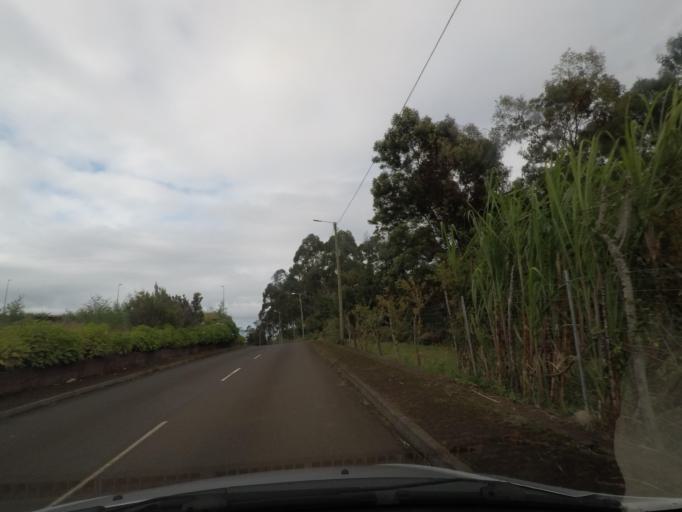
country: PT
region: Madeira
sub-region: Santana
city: Santana
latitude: 32.7858
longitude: -16.8787
